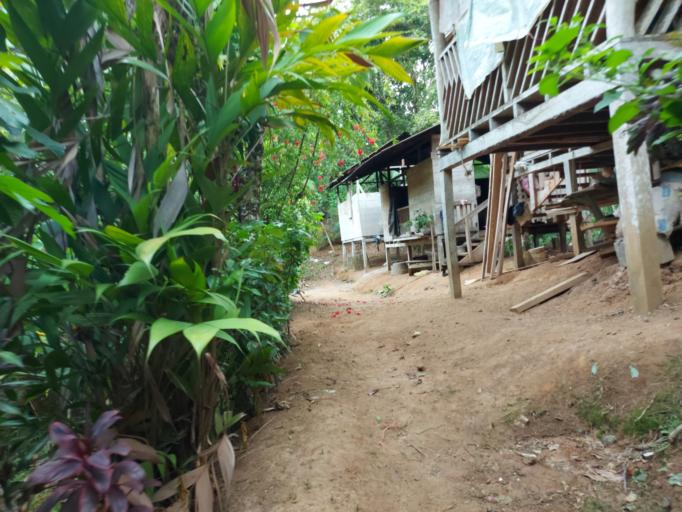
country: PA
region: Bocas del Toro
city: Barranco
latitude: 9.6393
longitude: -82.7828
